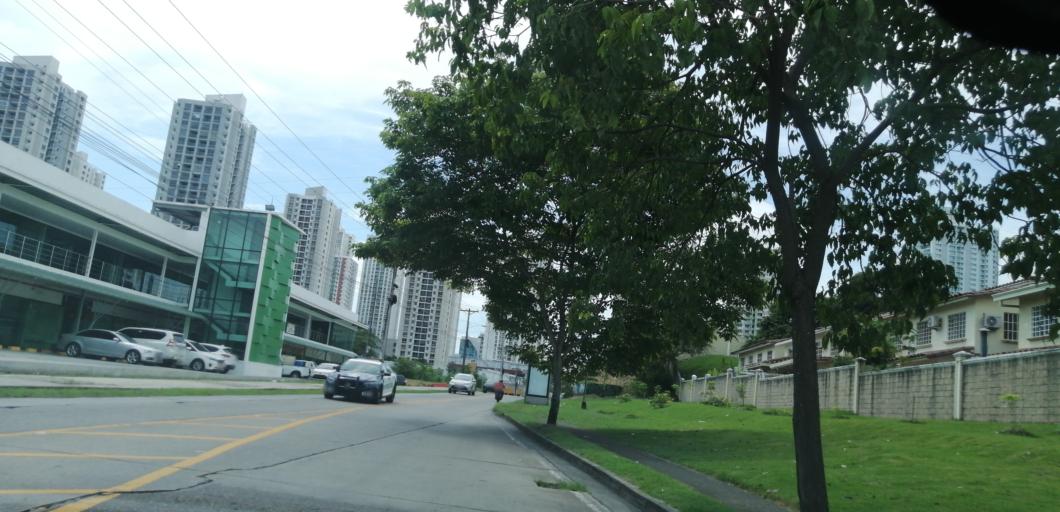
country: PA
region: Panama
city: Panama
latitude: 9.0316
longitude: -79.5265
